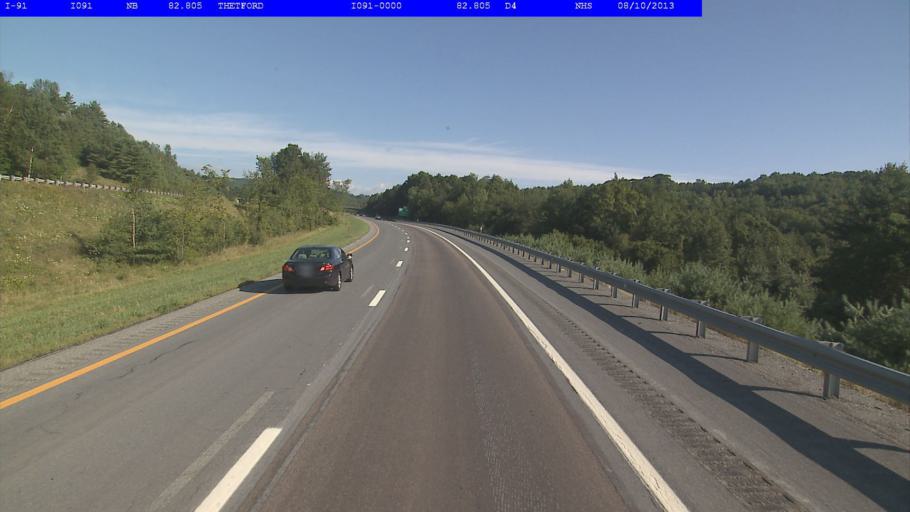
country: US
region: New Hampshire
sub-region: Grafton County
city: Lyme
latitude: 43.7932
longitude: -72.2144
